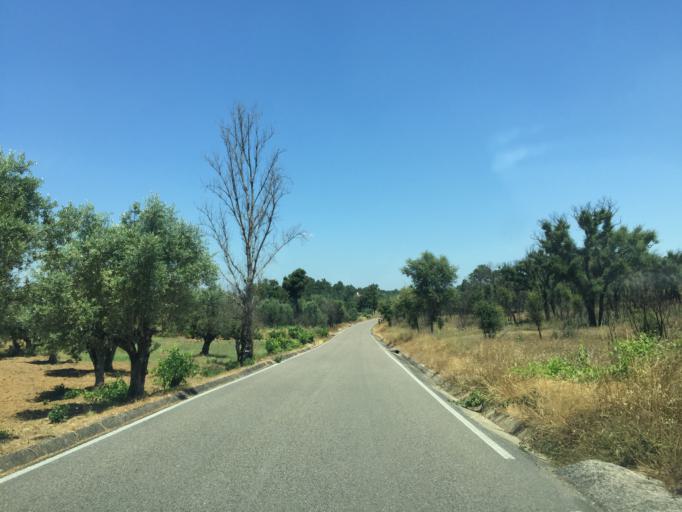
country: PT
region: Santarem
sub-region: Tomar
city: Tomar
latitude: 39.5905
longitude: -8.3279
